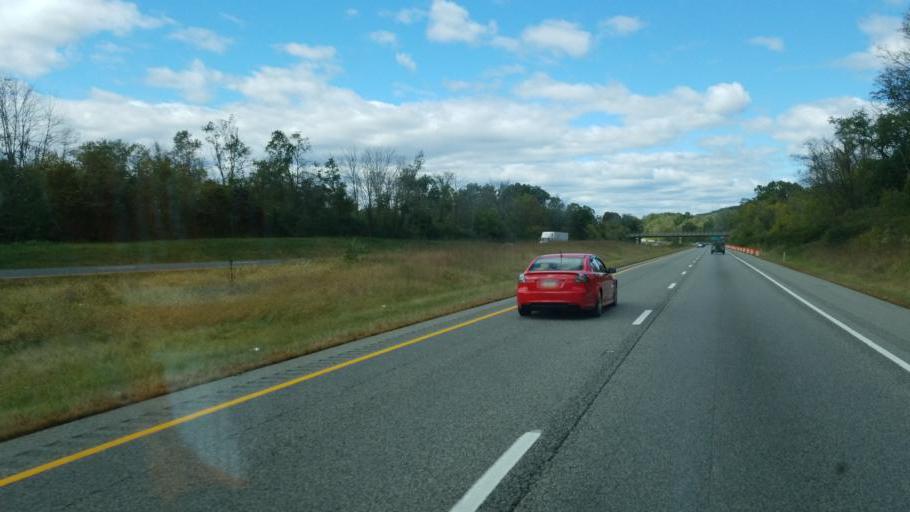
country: US
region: Maryland
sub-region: Washington County
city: Hancock
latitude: 39.6343
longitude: -78.0236
